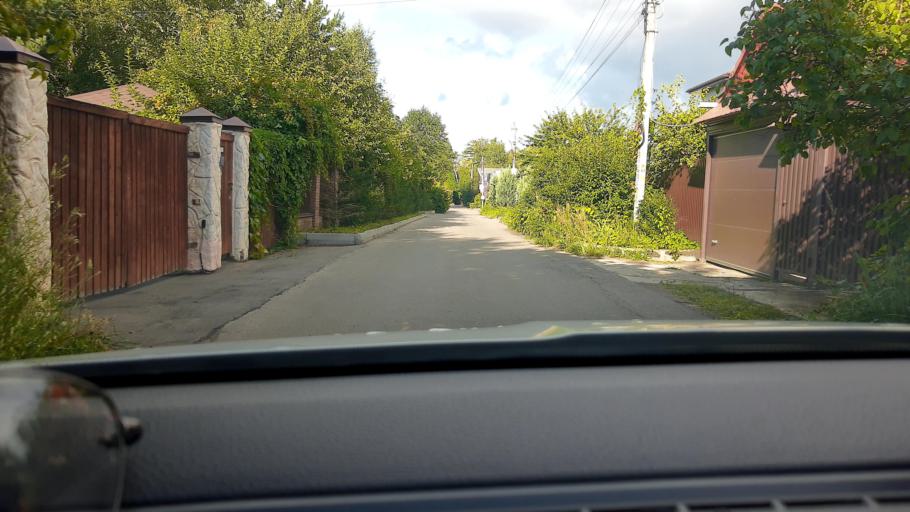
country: RU
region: Moskovskaya
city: Nemchinovka
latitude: 55.7149
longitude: 37.3611
